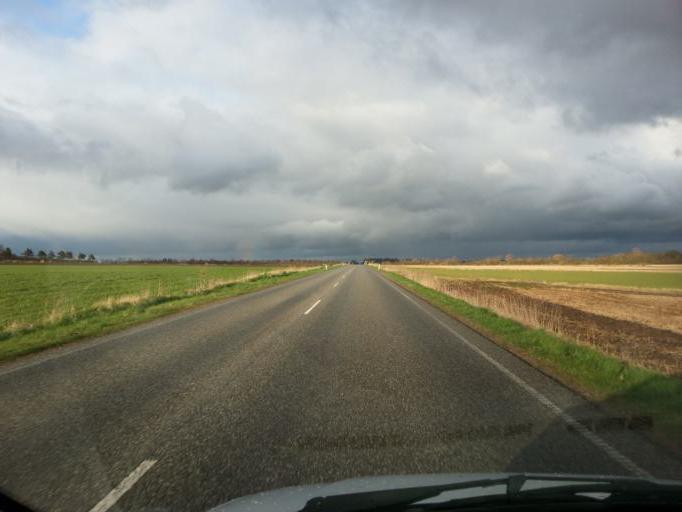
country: DK
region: Central Jutland
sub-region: Holstebro Kommune
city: Ulfborg
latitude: 56.2949
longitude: 8.3540
